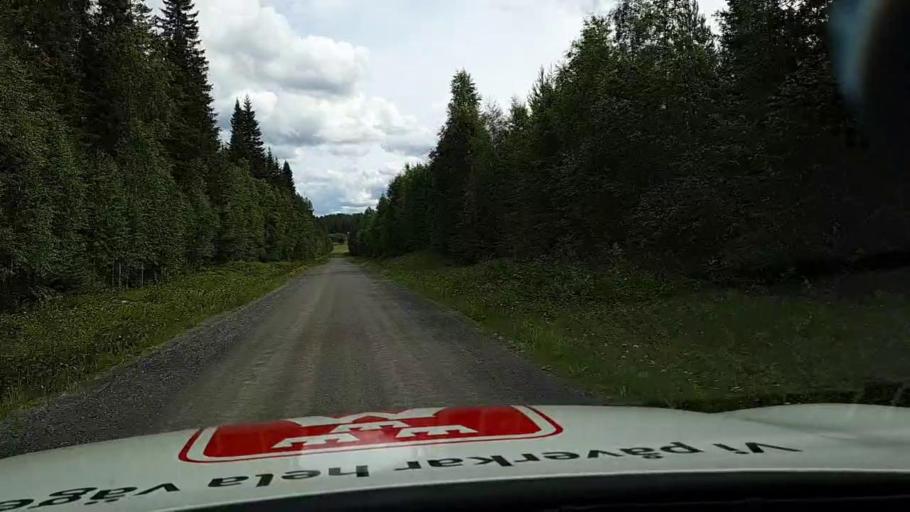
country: SE
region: Jaemtland
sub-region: Braecke Kommun
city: Braecke
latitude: 63.2874
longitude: 15.3602
